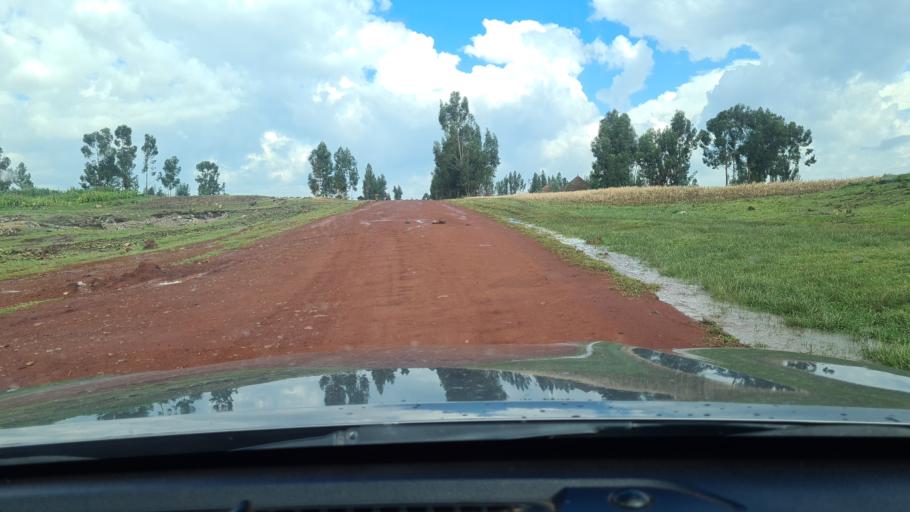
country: ET
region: Oromiya
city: Huruta
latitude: 8.0075
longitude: 39.5691
